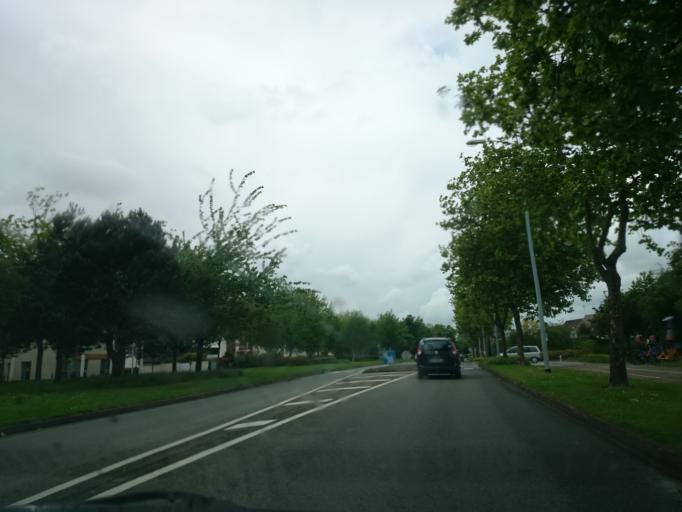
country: FR
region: Brittany
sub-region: Departement du Morbihan
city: Vannes
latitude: 47.6504
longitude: -2.7830
